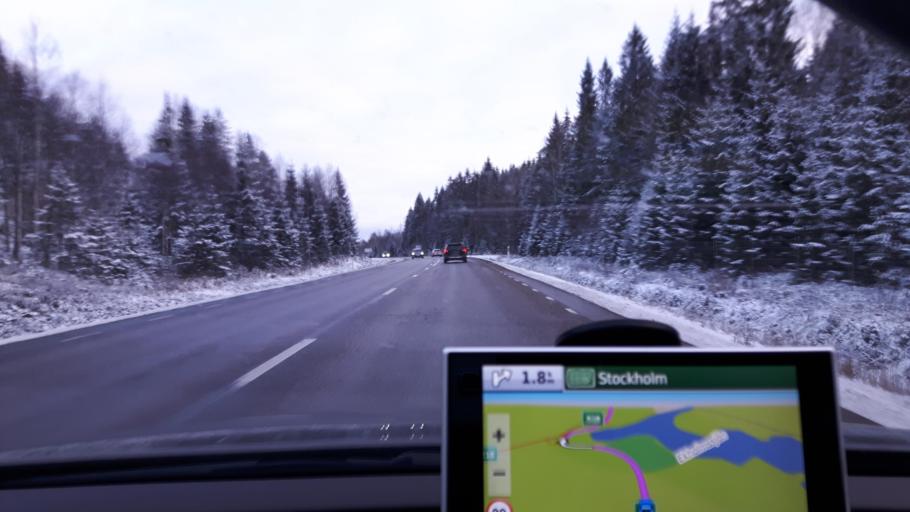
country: SE
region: Vaermland
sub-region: Grums Kommun
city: Slottsbron
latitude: 59.2424
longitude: 13.0032
